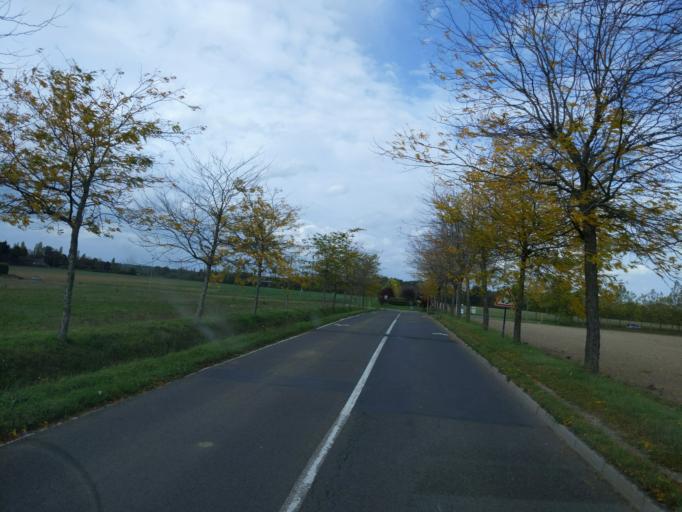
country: FR
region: Ile-de-France
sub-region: Departement des Yvelines
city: Rambouillet
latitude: 48.6500
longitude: 1.8471
